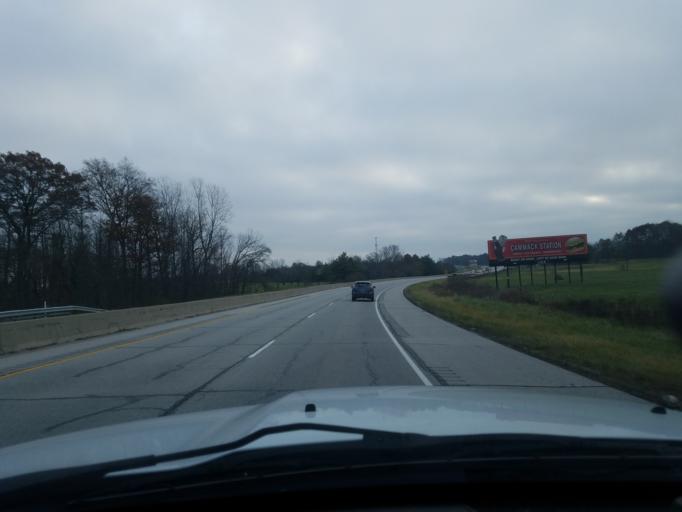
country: US
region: Indiana
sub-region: Delaware County
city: Yorktown
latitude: 40.2220
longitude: -85.5248
